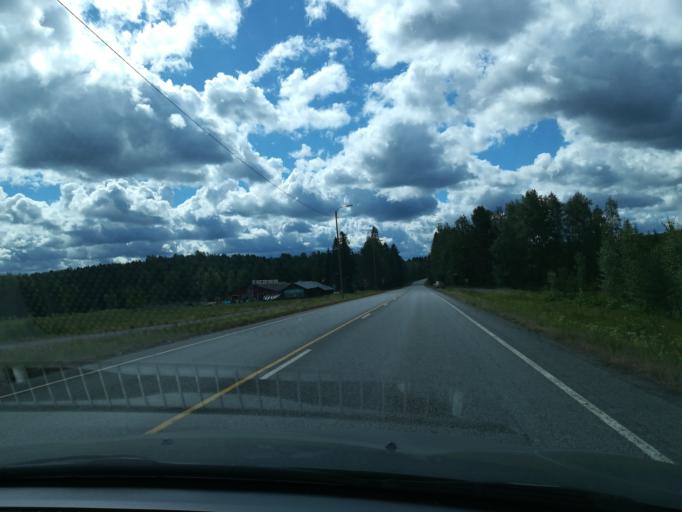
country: FI
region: Southern Savonia
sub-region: Mikkeli
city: Ristiina
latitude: 61.4795
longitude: 27.2522
